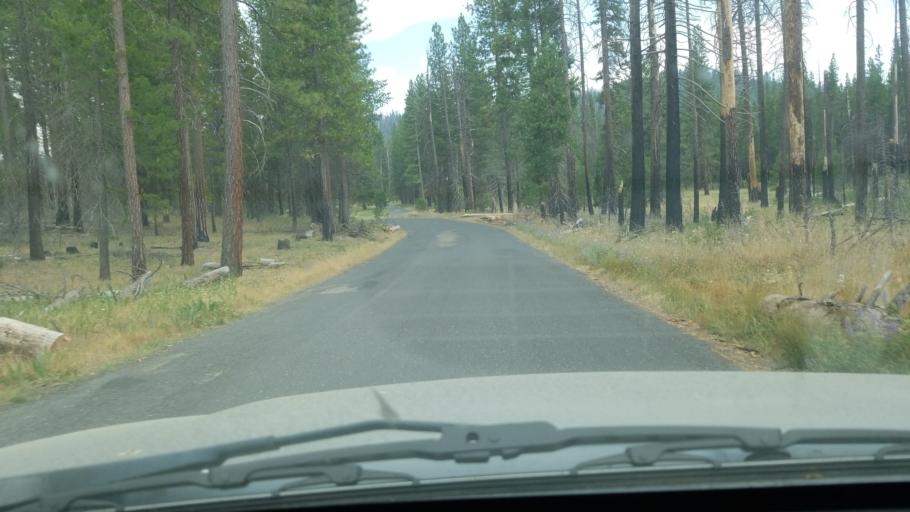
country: US
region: California
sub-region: Mariposa County
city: Yosemite Valley
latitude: 37.8380
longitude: -119.8490
